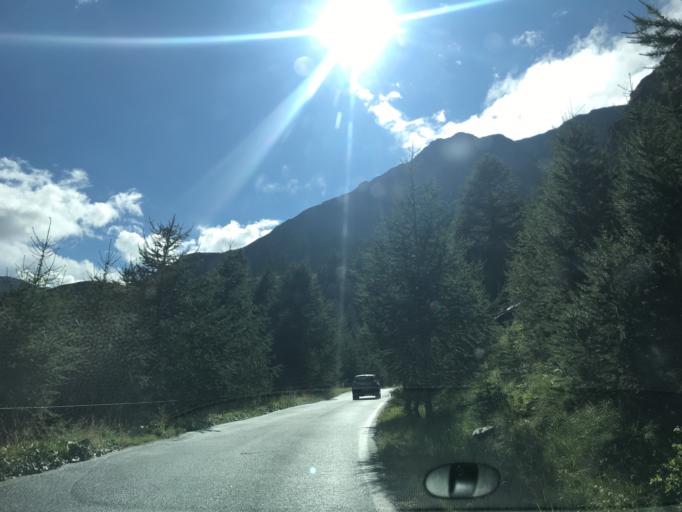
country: IT
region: Piedmont
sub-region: Provincia di Cuneo
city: Pontechianale
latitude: 44.6608
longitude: 6.9898
